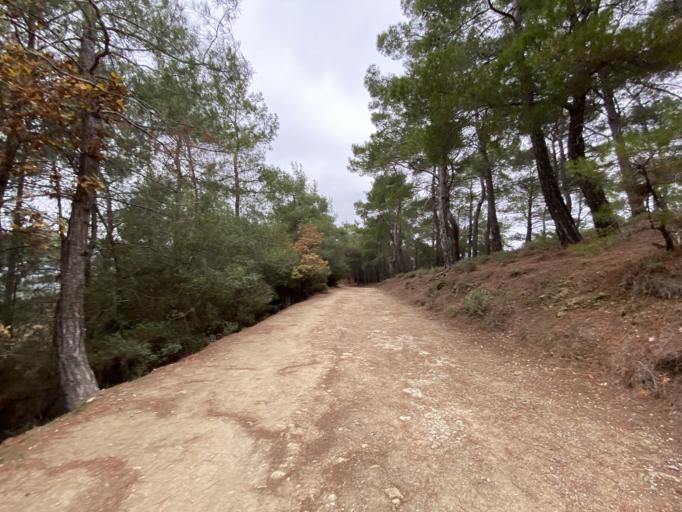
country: TR
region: Canakkale
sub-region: Merkez
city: Kucukkuyu
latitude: 39.5614
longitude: 26.6176
